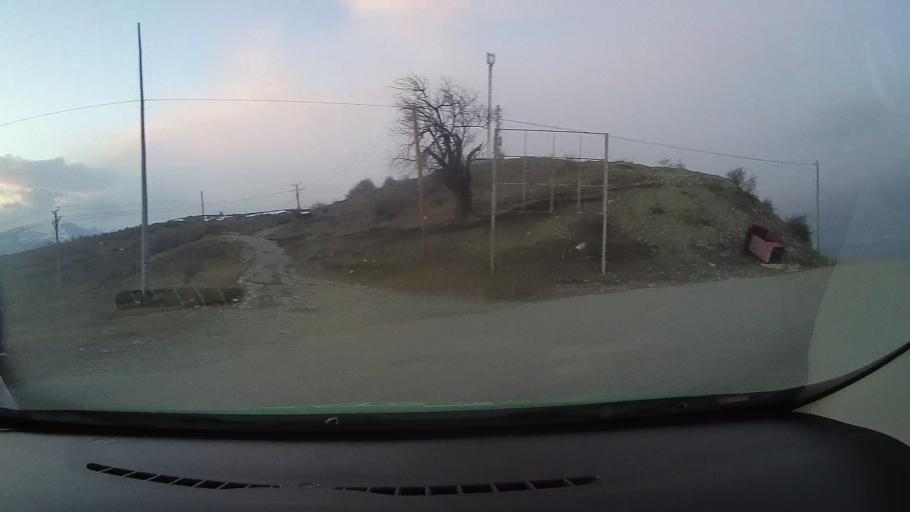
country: RO
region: Prahova
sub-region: Comuna Secaria
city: Secaria
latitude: 45.2834
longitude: 25.7014
